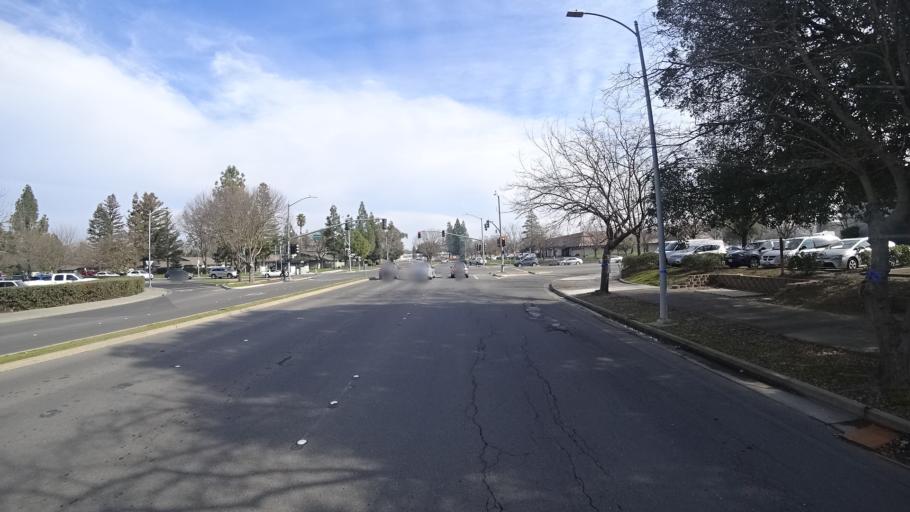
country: US
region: California
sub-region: Yolo County
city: Davis
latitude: 38.5487
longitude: -121.7272
